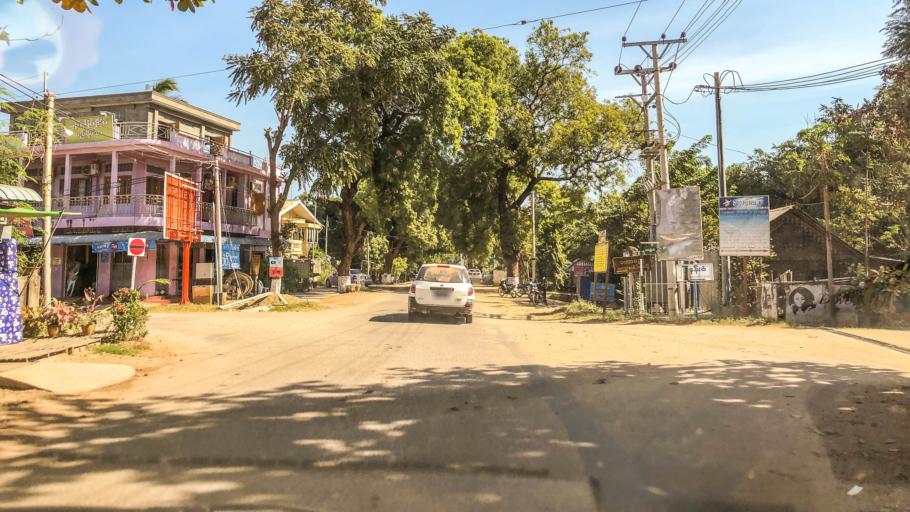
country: MM
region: Magway
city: Magway
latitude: 19.9661
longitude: 95.0385
